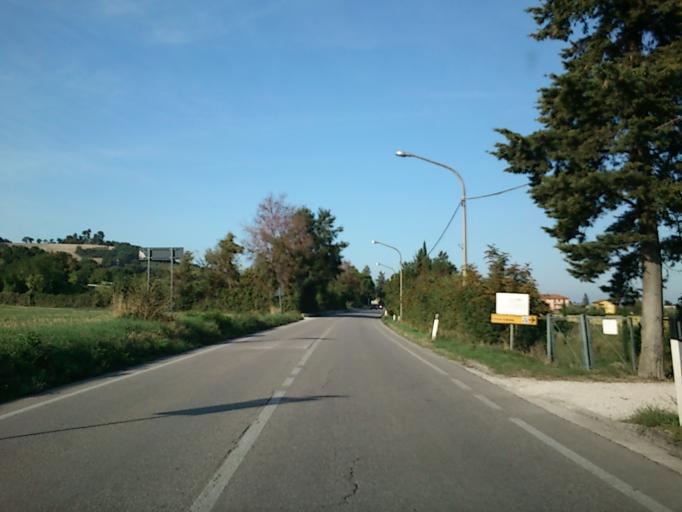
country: IT
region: The Marches
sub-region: Provincia di Pesaro e Urbino
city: Fossombrone
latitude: 43.6985
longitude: 12.8287
